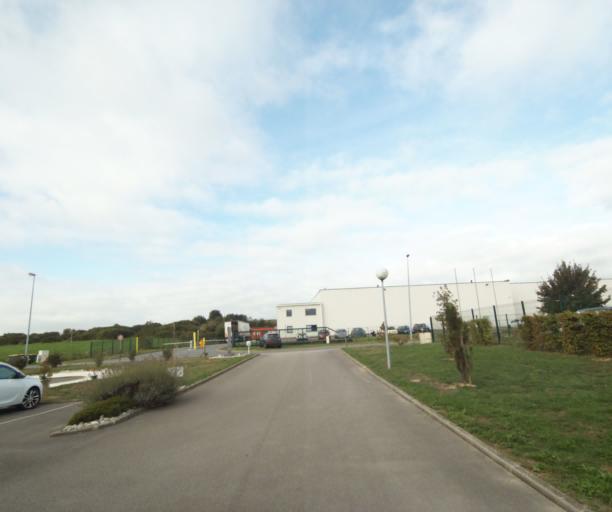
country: FR
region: Nord-Pas-de-Calais
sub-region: Departement du Pas-de-Calais
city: Etaples
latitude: 50.5156
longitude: 1.6666
